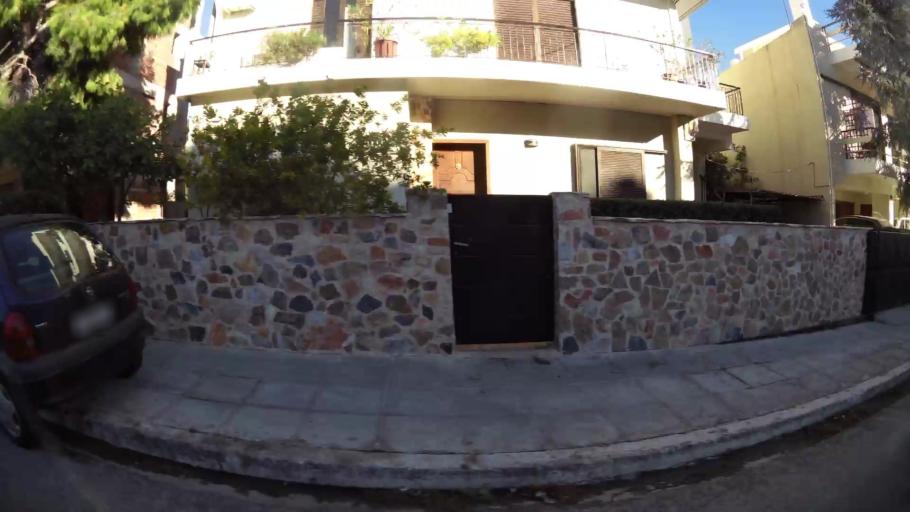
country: GR
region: Attica
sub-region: Nomarchia Anatolikis Attikis
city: Paiania
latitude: 37.9593
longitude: 23.8525
